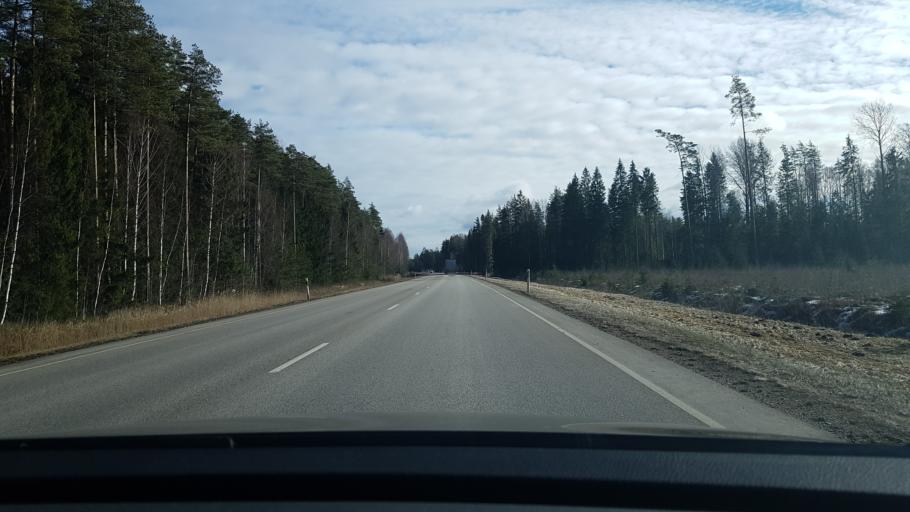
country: EE
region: Paernumaa
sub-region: Saarde vald
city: Kilingi-Nomme
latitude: 58.1651
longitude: 24.8303
